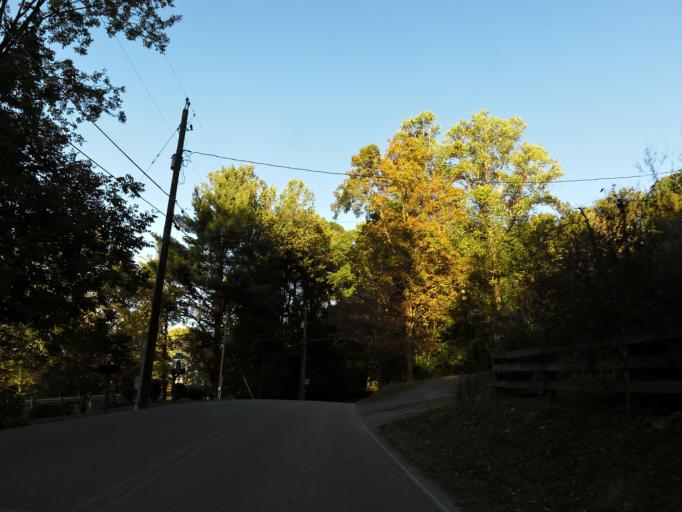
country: US
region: Tennessee
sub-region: Knox County
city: Knoxville
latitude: 36.0519
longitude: -83.9355
